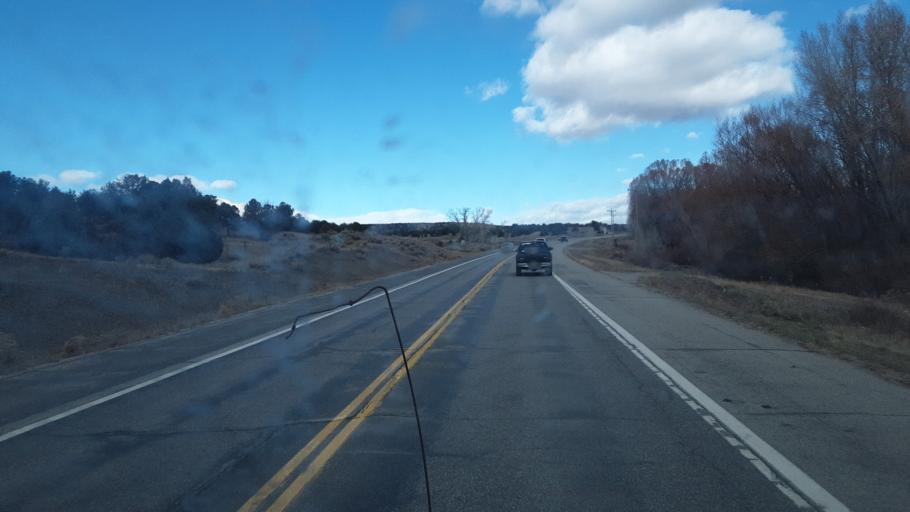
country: US
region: Colorado
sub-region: Chaffee County
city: Salida
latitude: 38.6365
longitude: -106.0811
